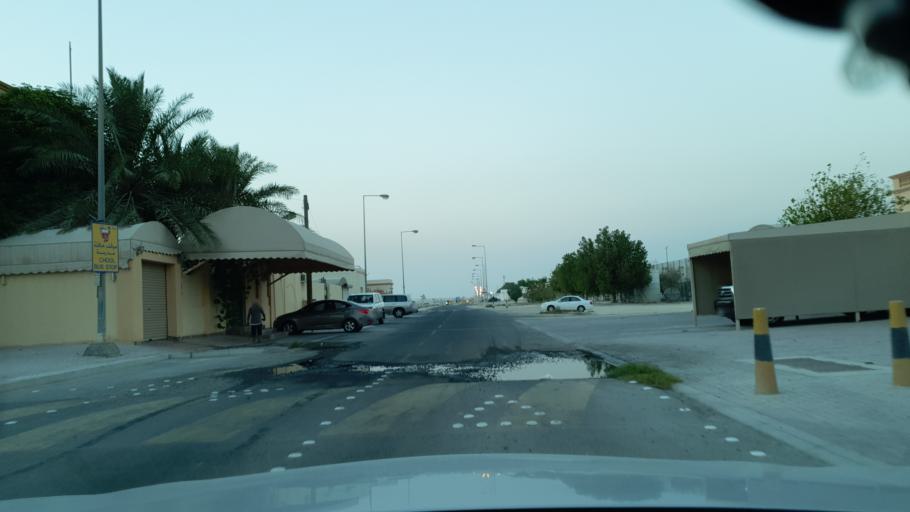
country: BH
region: Central Governorate
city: Dar Kulayb
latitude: 25.9792
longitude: 50.6152
